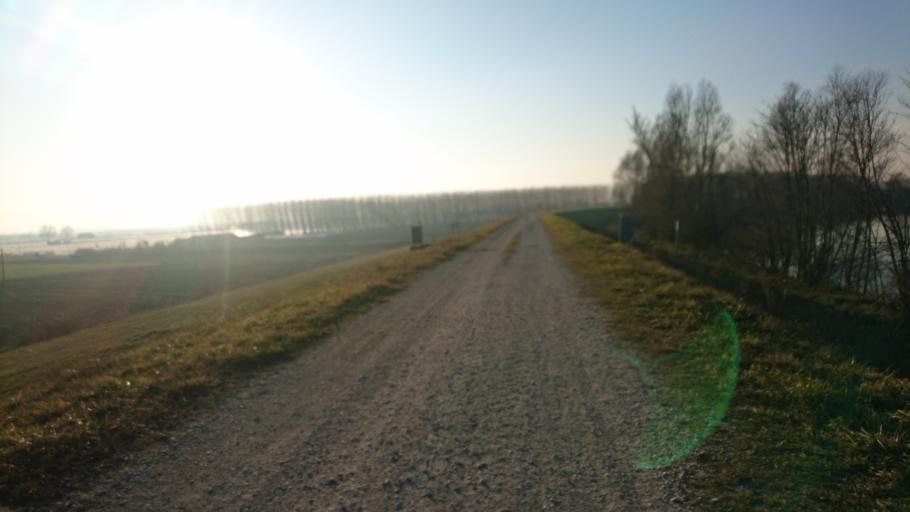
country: IT
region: Veneto
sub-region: Provincia di Rovigo
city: Mardimago
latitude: 45.1205
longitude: 11.8252
